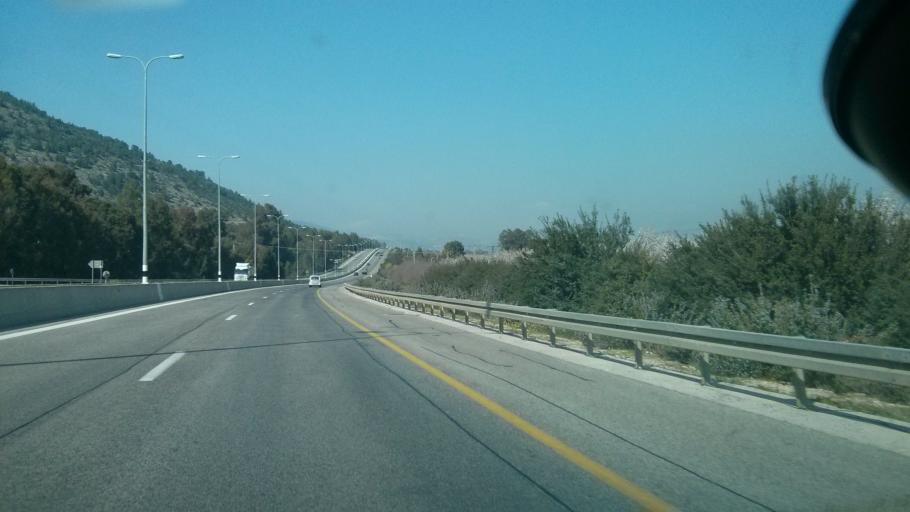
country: IL
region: Northern District
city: Rosh Pinna
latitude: 33.0801
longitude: 35.5752
